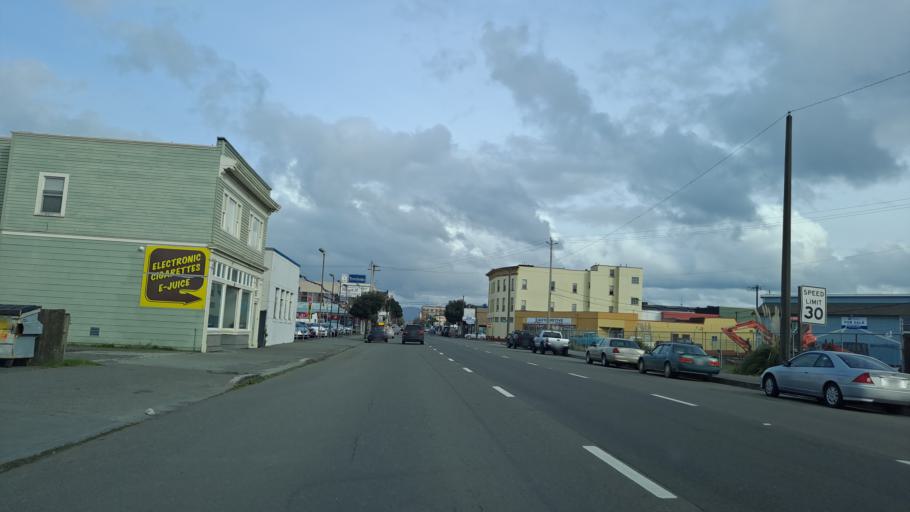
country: US
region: California
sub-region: Humboldt County
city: Eureka
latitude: 40.8010
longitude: -124.1729
